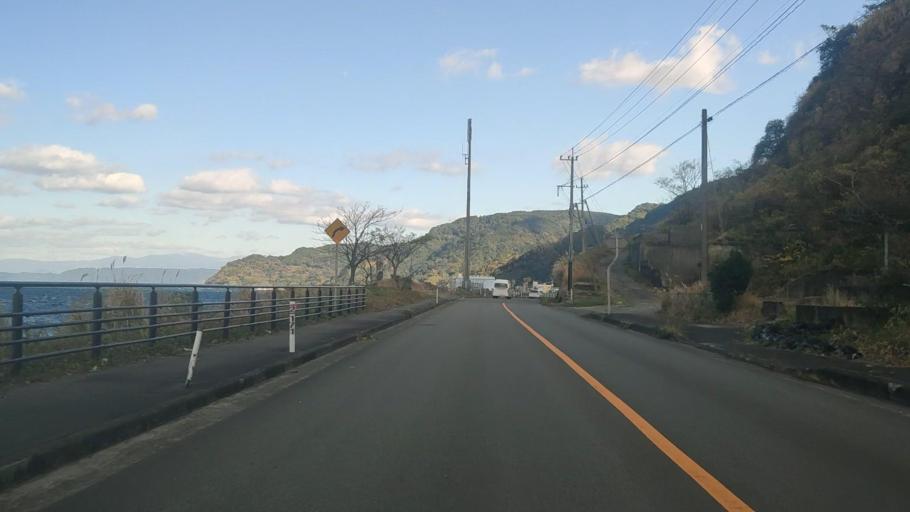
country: JP
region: Kagoshima
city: Tarumizu
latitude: 31.5764
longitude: 130.7797
